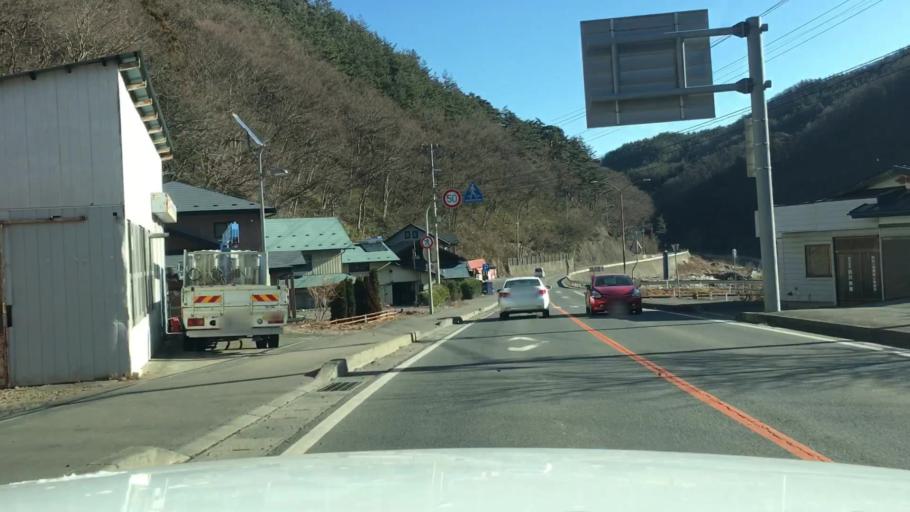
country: JP
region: Iwate
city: Miyako
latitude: 39.5998
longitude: 141.6805
